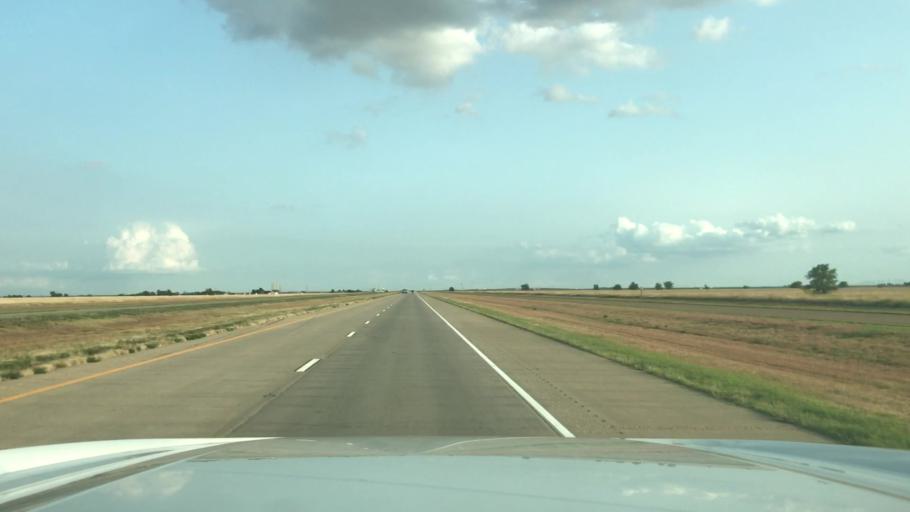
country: US
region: Texas
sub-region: Swisher County
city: Tulia
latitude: 34.5098
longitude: -101.7909
